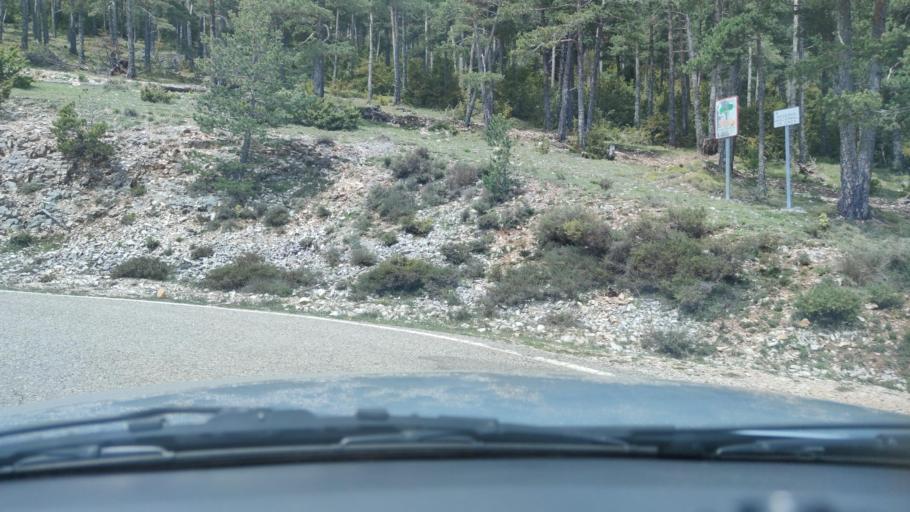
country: ES
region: Catalonia
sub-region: Provincia de Lleida
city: Gosol
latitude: 42.1859
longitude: 1.5583
